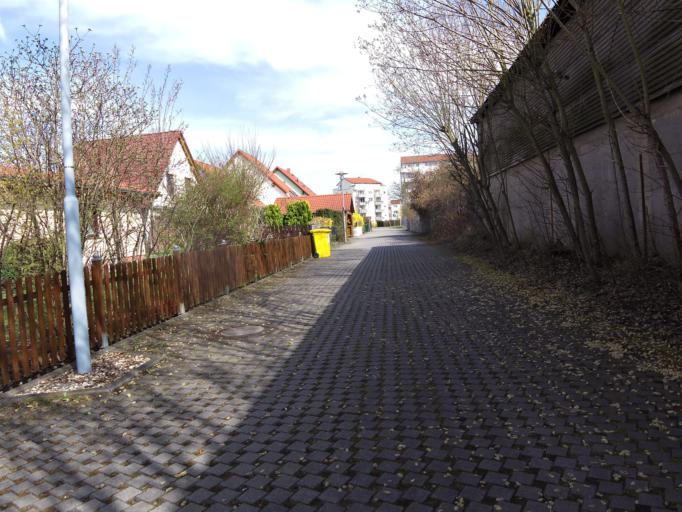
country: DE
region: Saxony
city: Schkeuditz
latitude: 51.3584
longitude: 12.2805
